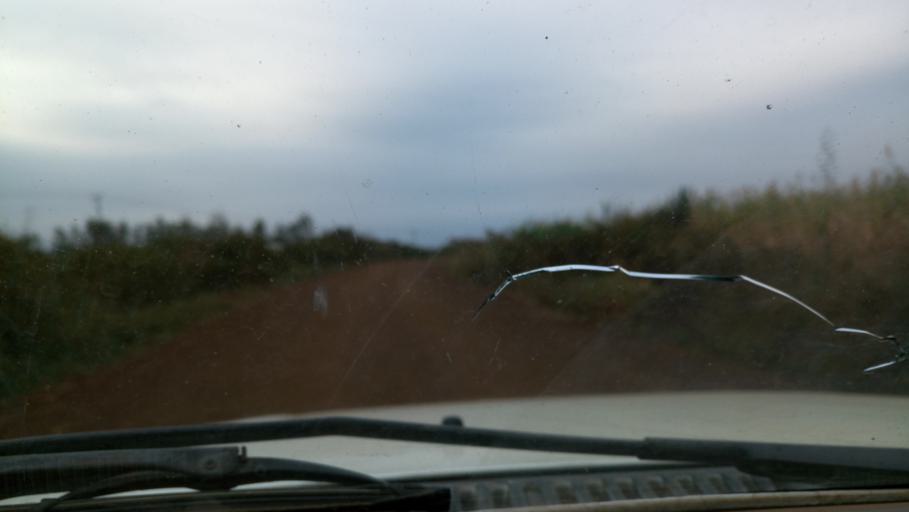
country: KE
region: Murang'a District
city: Maragua
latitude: -0.7757
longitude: 37.1580
